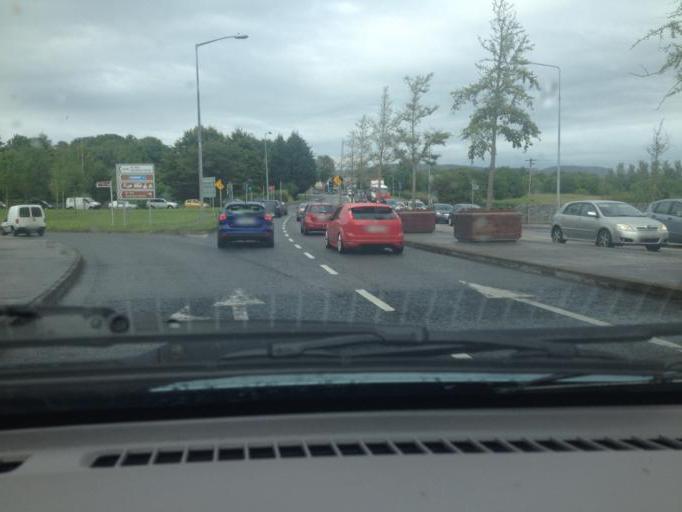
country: IE
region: Connaught
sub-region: Sligo
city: Sligo
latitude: 54.2779
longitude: -8.4750
